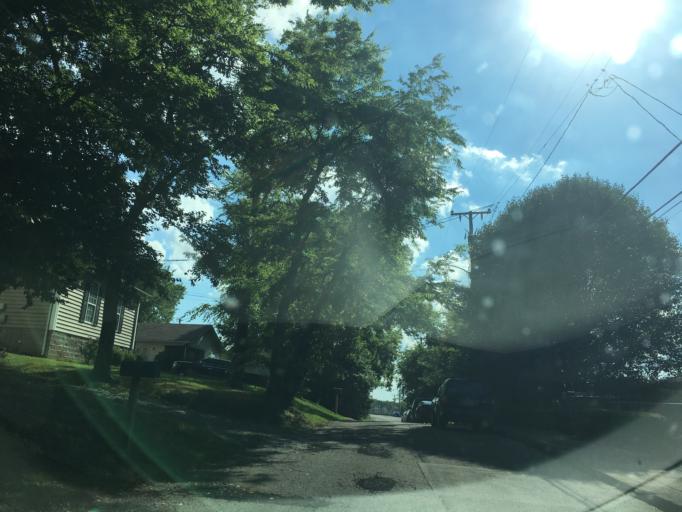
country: US
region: Tennessee
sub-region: Davidson County
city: Nashville
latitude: 36.1582
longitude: -86.8255
